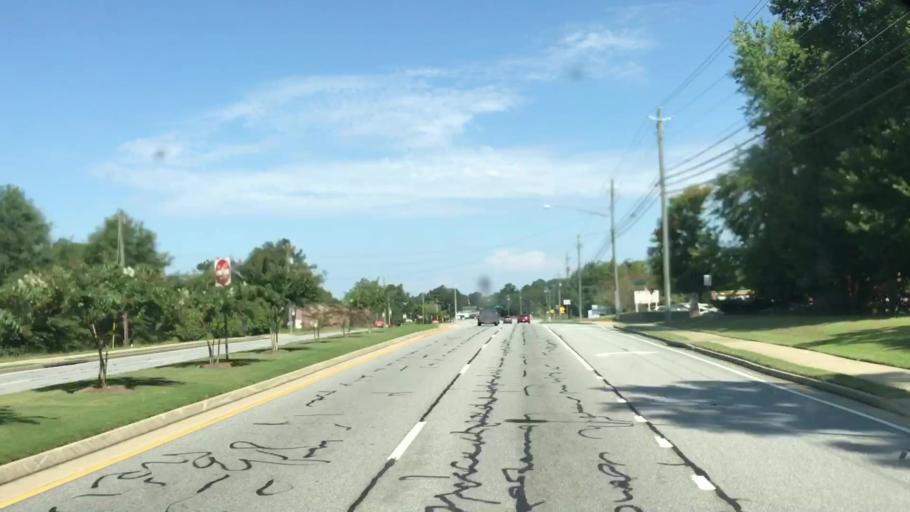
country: US
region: Georgia
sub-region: Gwinnett County
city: Grayson
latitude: 33.8889
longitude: -83.9475
